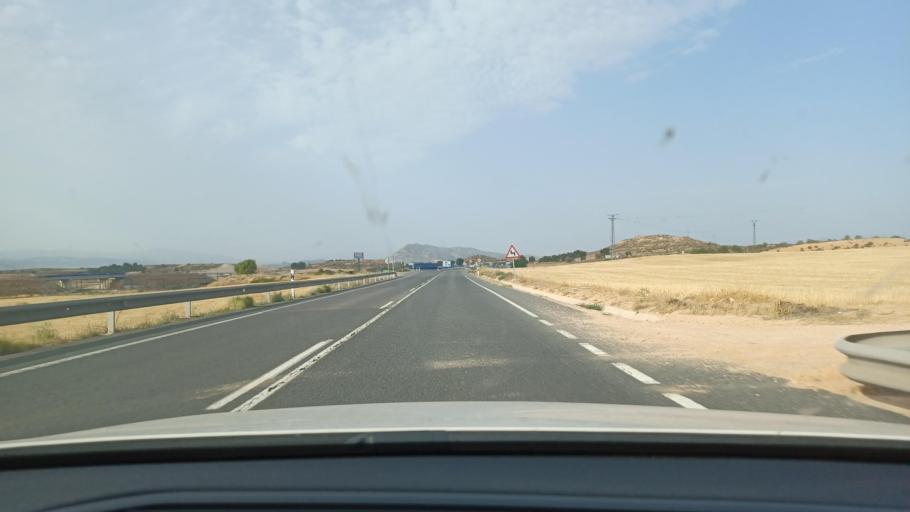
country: ES
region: Castille-La Mancha
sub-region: Provincia de Albacete
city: Caudete
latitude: 38.7355
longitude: -0.9347
